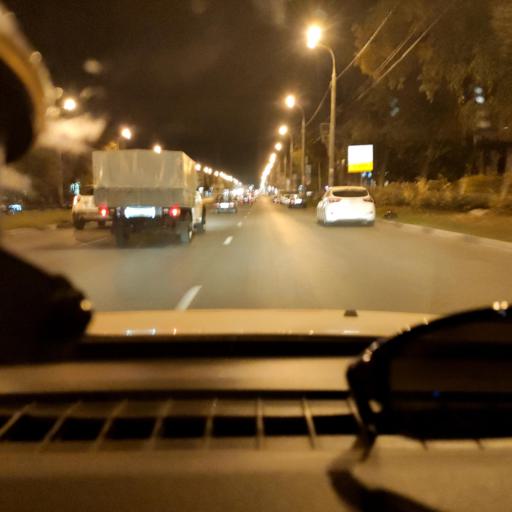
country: RU
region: Samara
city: Samara
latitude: 53.2007
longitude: 50.1955
